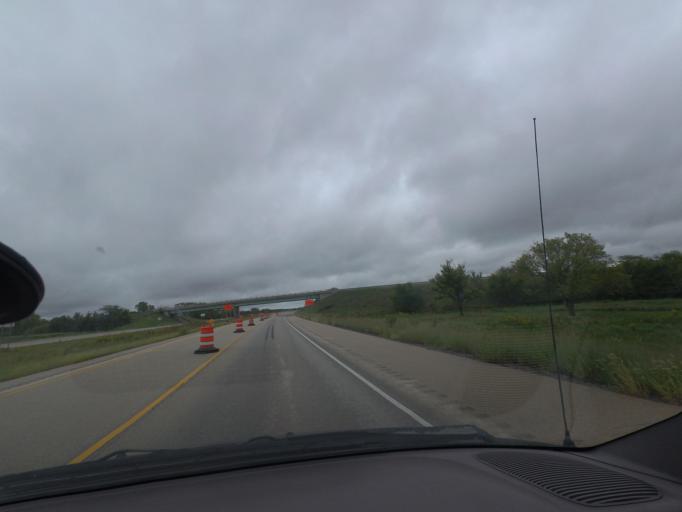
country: US
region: Illinois
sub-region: Piatt County
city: Cerro Gordo
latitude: 39.9749
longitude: -88.8047
